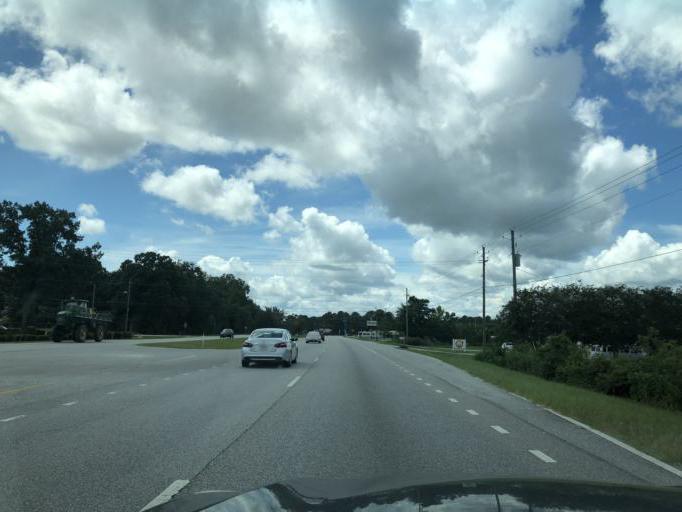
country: US
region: Alabama
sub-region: Barbour County
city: Eufaula
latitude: 31.9210
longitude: -85.1466
